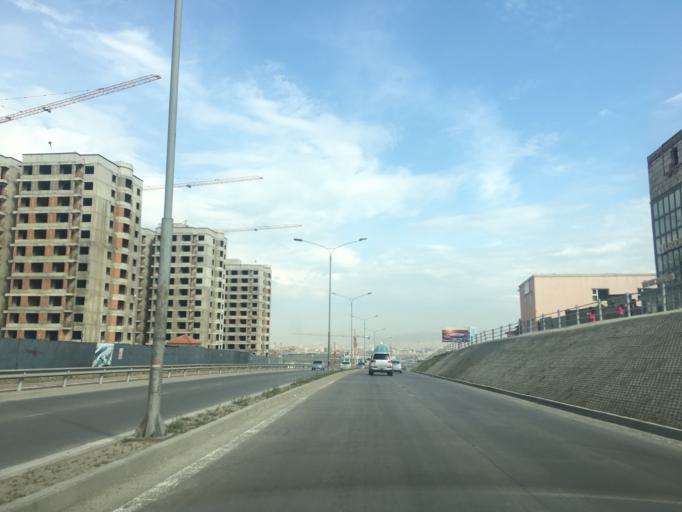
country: MN
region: Ulaanbaatar
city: Ulaanbaatar
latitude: 47.8674
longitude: 106.7862
